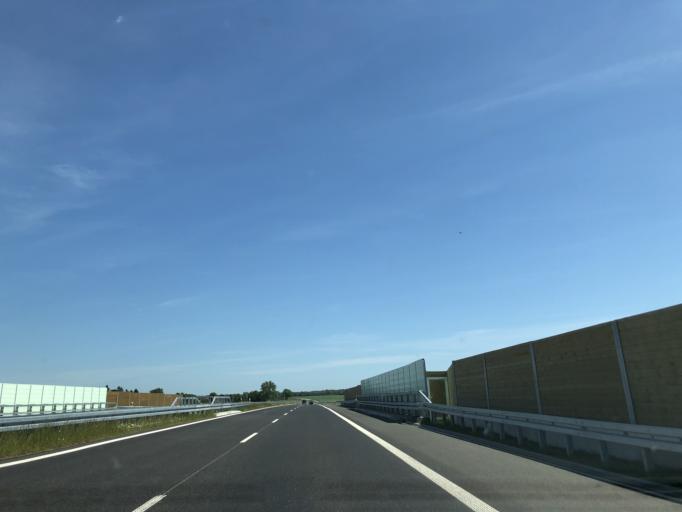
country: PL
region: West Pomeranian Voivodeship
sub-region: Powiat goleniowski
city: Osina
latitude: 53.6398
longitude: 15.0390
